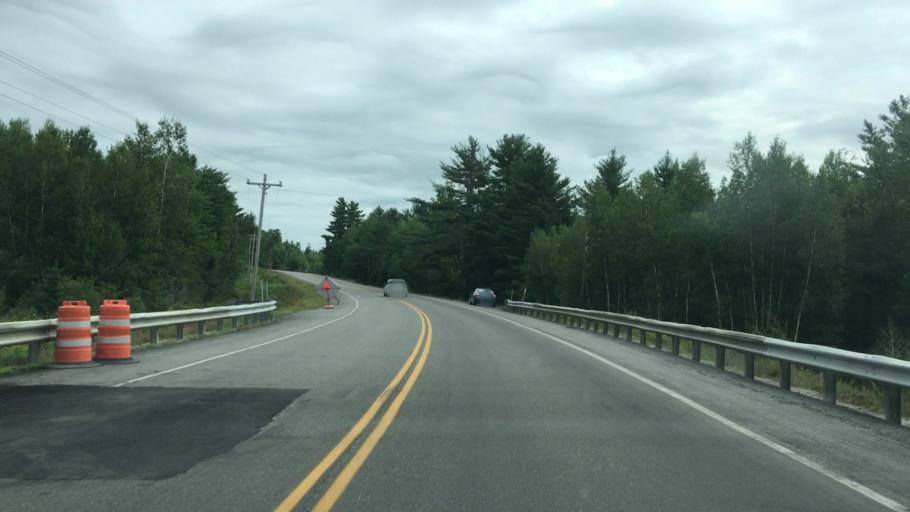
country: US
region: Maine
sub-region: Washington County
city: Machias
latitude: 44.9995
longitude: -67.5856
